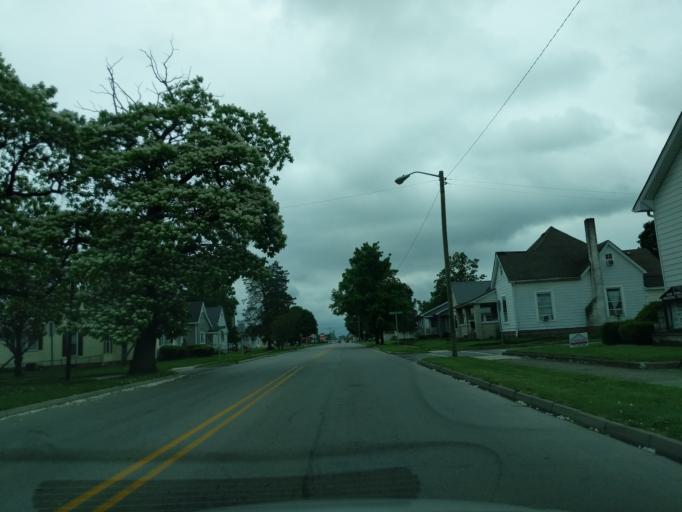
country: US
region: Indiana
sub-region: Madison County
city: Elwood
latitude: 40.2770
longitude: -85.8270
